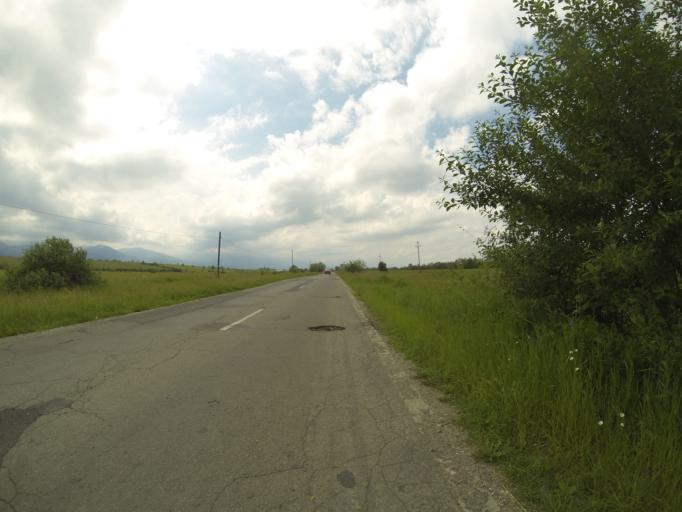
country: RO
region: Brasov
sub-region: Comuna Sinca Veche
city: Sinca Veche
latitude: 45.7581
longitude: 25.1434
